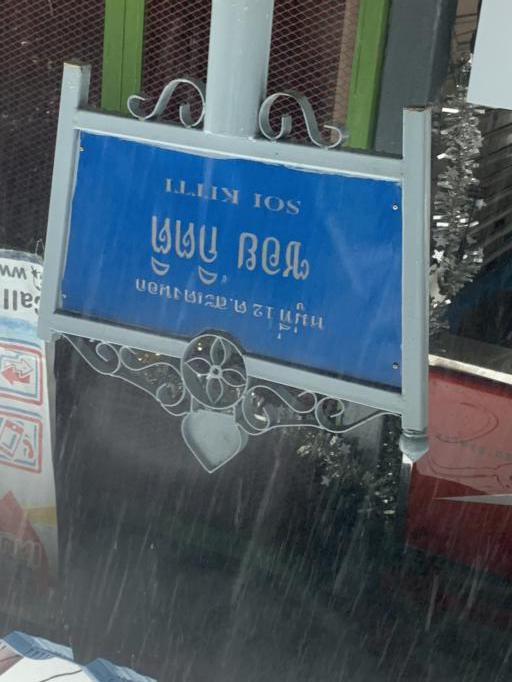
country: TH
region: Yala
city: Yala
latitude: 6.5372
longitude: 101.2901
